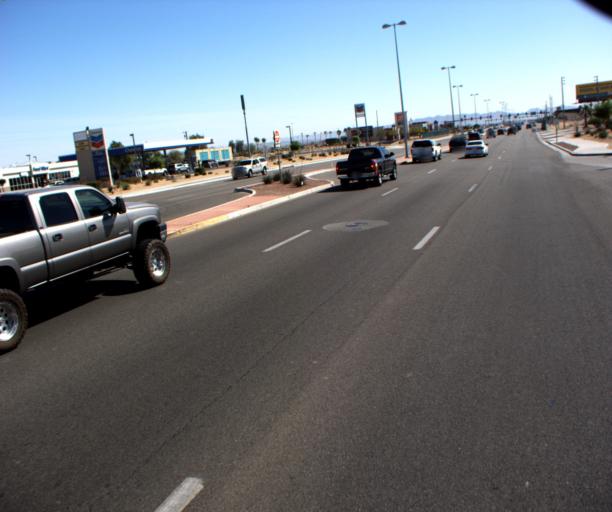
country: US
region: Arizona
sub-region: Yuma County
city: Yuma
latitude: 32.6984
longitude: -114.6143
